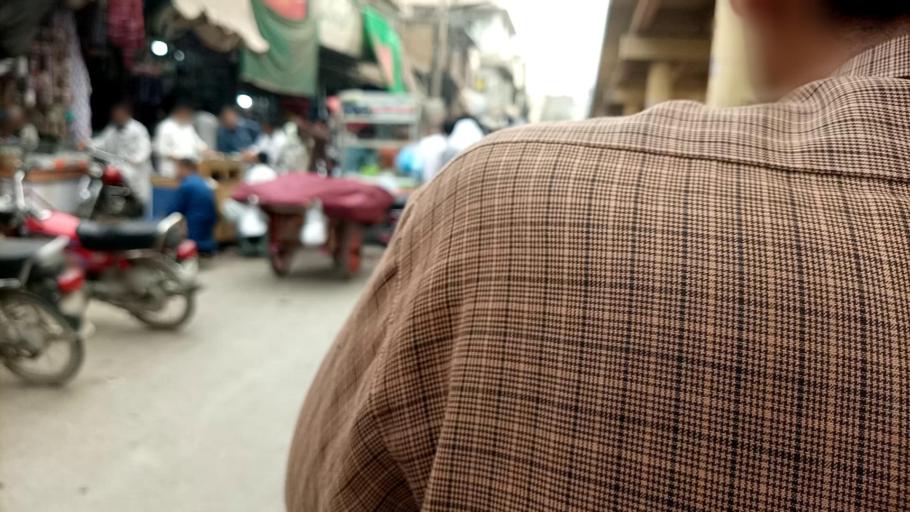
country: PK
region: Khyber Pakhtunkhwa
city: Peshawar
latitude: 34.0172
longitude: 71.5802
